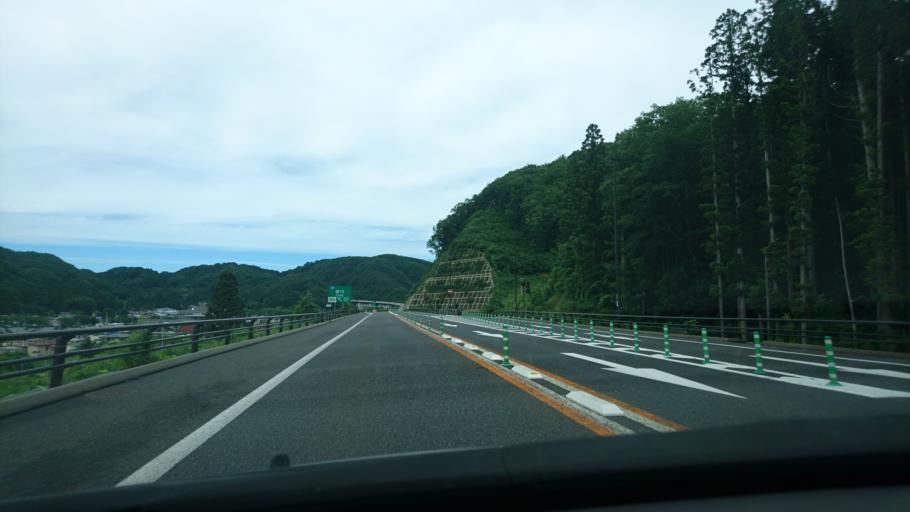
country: JP
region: Iwate
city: Miyako
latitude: 39.9994
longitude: 141.8858
